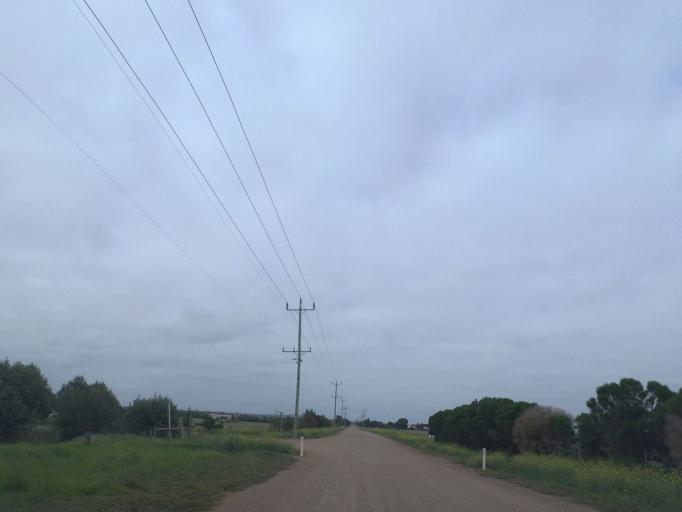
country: AU
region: Victoria
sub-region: Melton
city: Kurunjang
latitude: -37.6924
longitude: 144.6223
